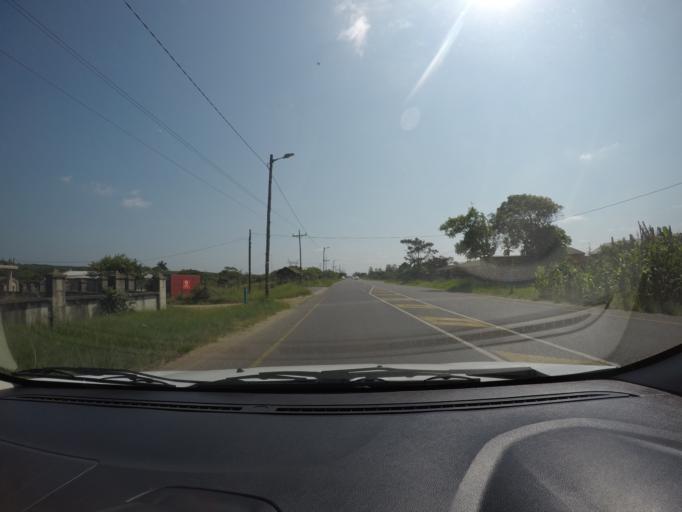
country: ZA
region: KwaZulu-Natal
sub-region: uThungulu District Municipality
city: eSikhawini
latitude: -28.8791
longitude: 31.8918
